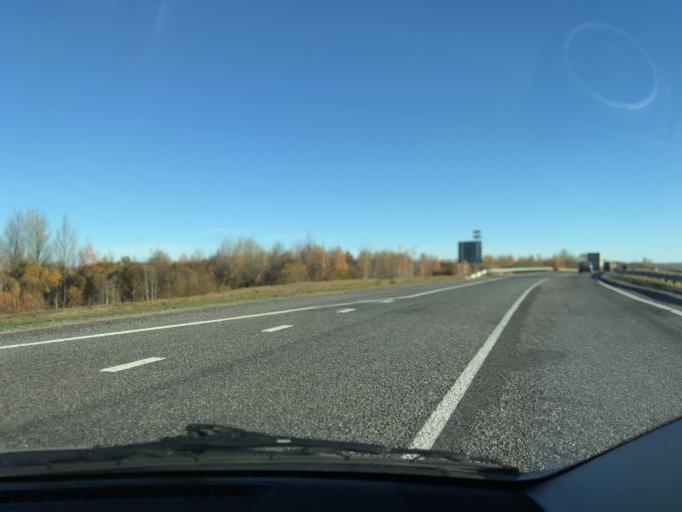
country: BY
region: Vitebsk
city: Vitebsk
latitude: 55.1059
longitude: 30.3037
